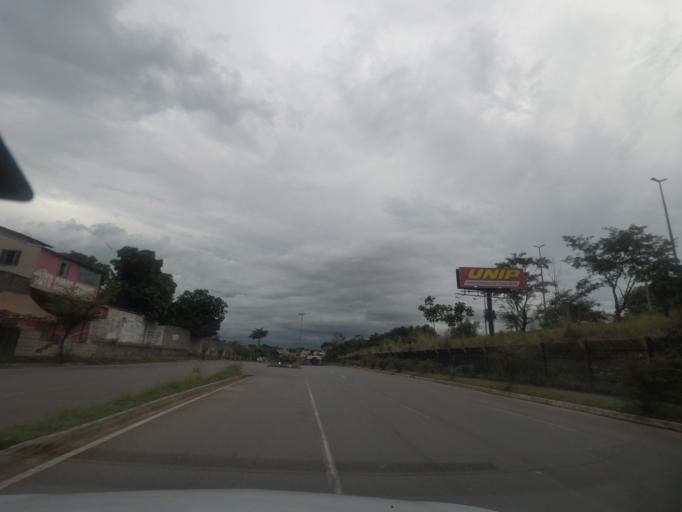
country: BR
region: Goias
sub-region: Goiania
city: Goiania
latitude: -16.7207
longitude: -49.2342
